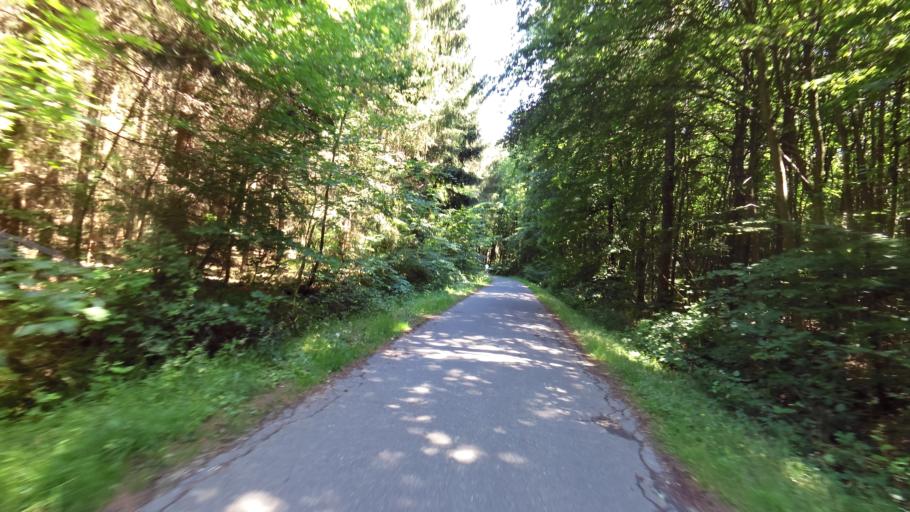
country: DE
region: North Rhine-Westphalia
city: Meckenheim
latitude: 50.6618
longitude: 7.0332
